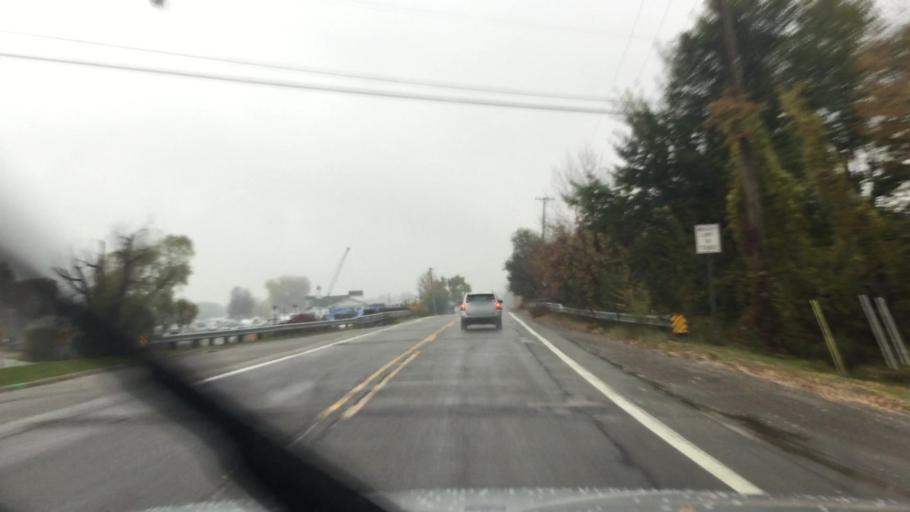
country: US
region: Michigan
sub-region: Macomb County
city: New Baltimore
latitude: 42.6582
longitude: -82.7760
